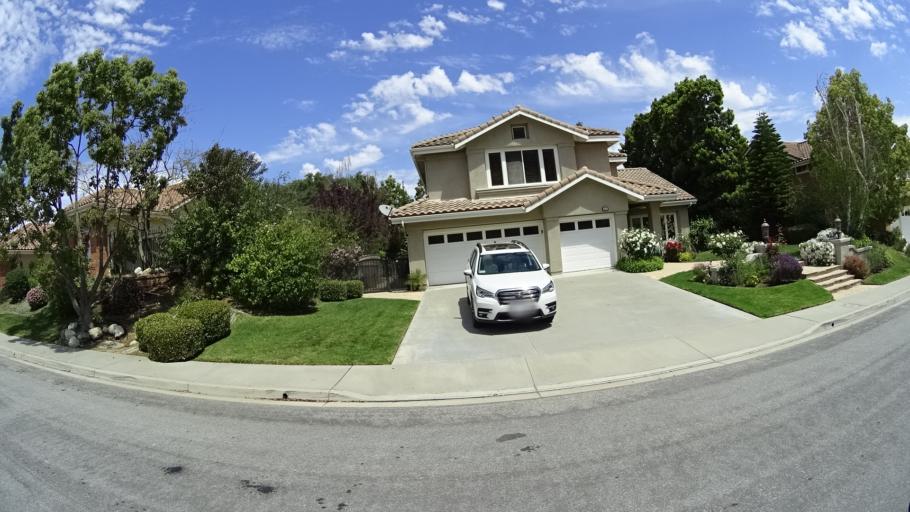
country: US
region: California
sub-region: Ventura County
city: Casa Conejo
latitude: 34.1727
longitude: -118.9171
